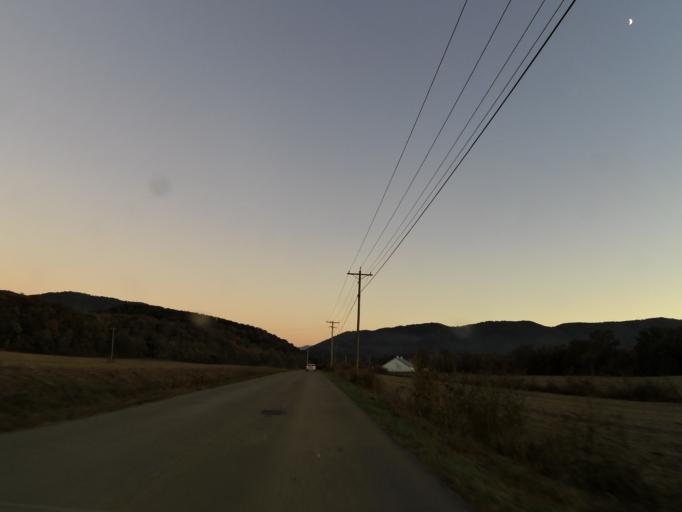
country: US
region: Tennessee
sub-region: Blount County
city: Wildwood
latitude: 35.7589
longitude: -83.8443
